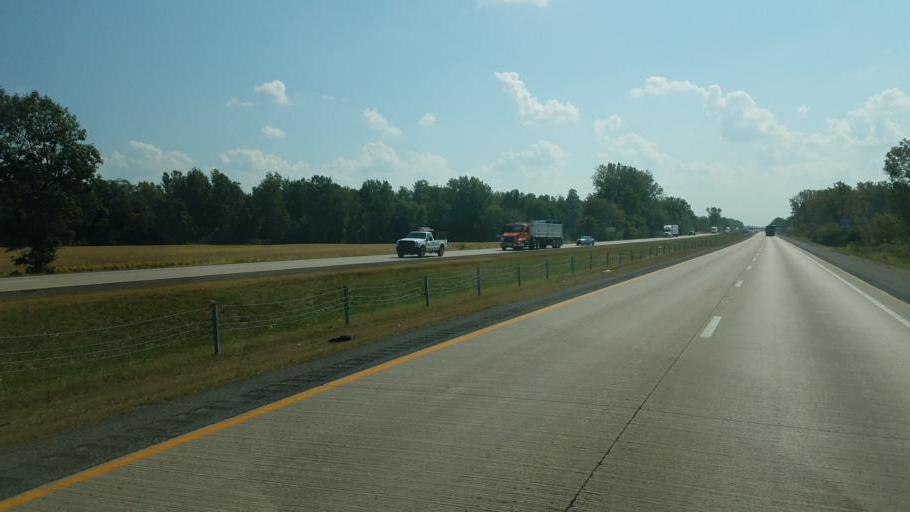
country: US
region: Indiana
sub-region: DeKalb County
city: Auburn
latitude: 41.3204
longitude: -85.0880
